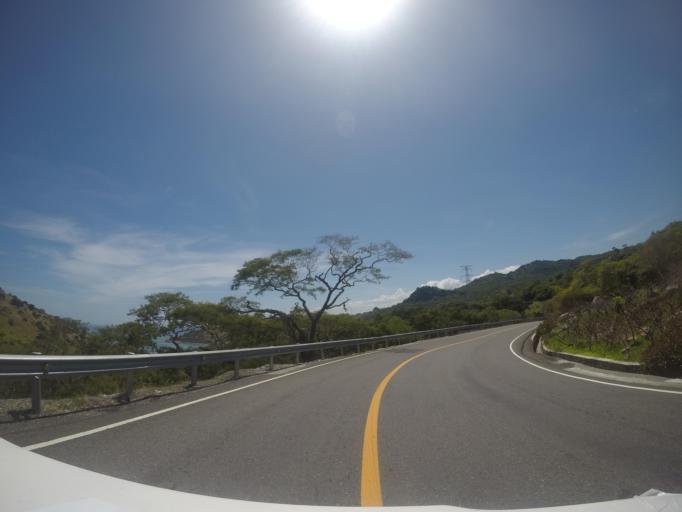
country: TL
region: Manatuto
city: Manatuto
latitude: -8.4904
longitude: 125.9610
